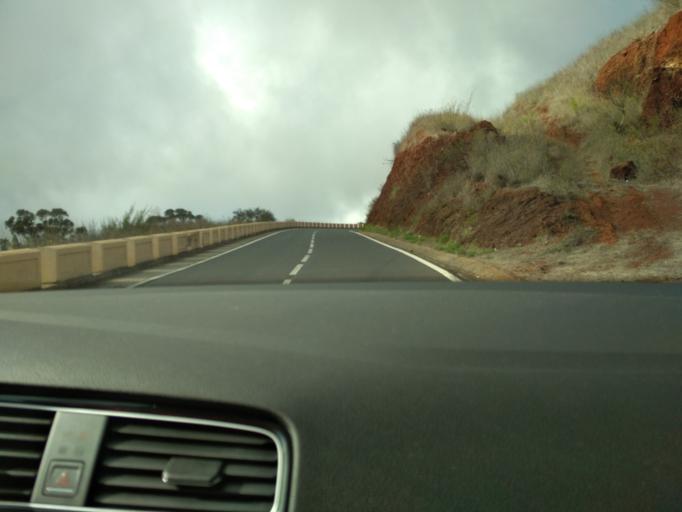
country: ES
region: Canary Islands
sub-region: Provincia de Santa Cruz de Tenerife
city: Santiago del Teide
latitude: 28.3203
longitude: -16.7972
